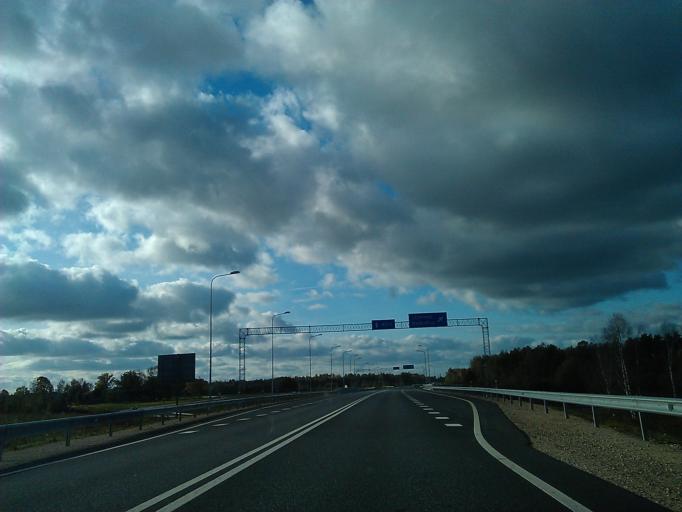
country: LV
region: Ogre
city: Jumprava
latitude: 56.7810
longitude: 25.0211
